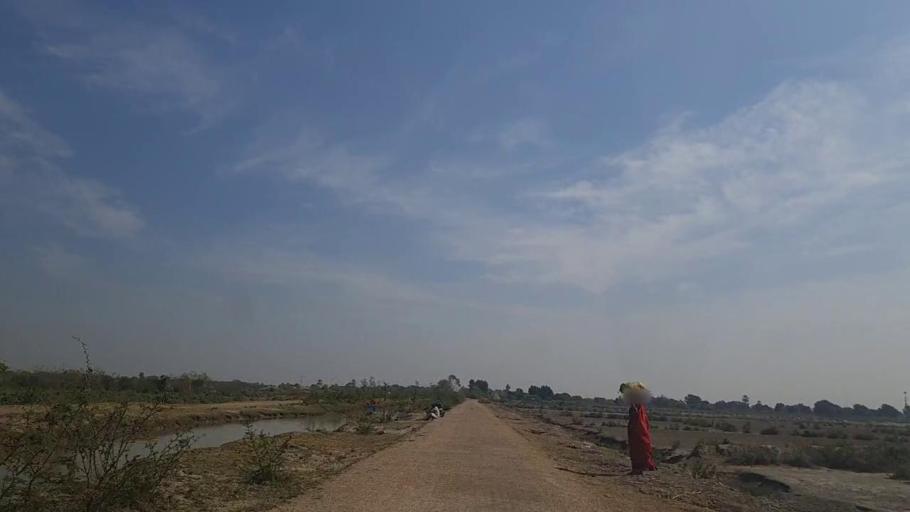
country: PK
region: Sindh
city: Mirpur Khas
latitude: 25.4672
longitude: 68.9534
